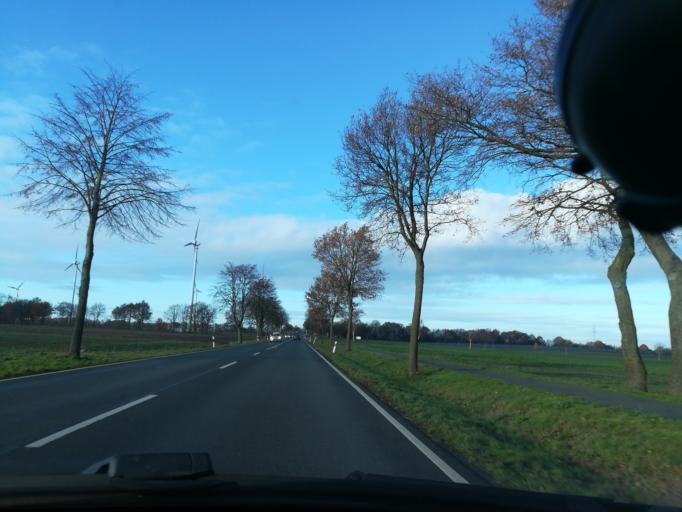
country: DE
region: Lower Saxony
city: Uchte
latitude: 52.4736
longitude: 8.9009
